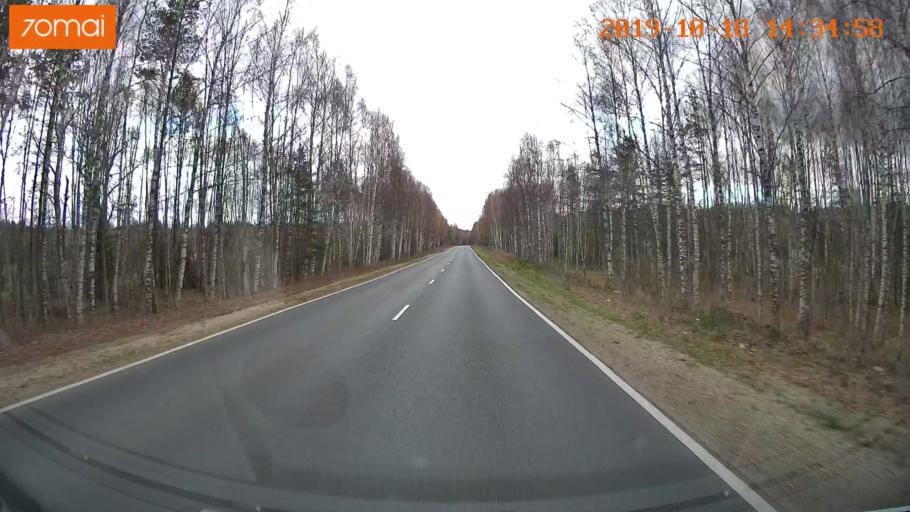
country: RU
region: Vladimir
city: Velikodvorskiy
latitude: 55.2181
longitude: 40.6268
